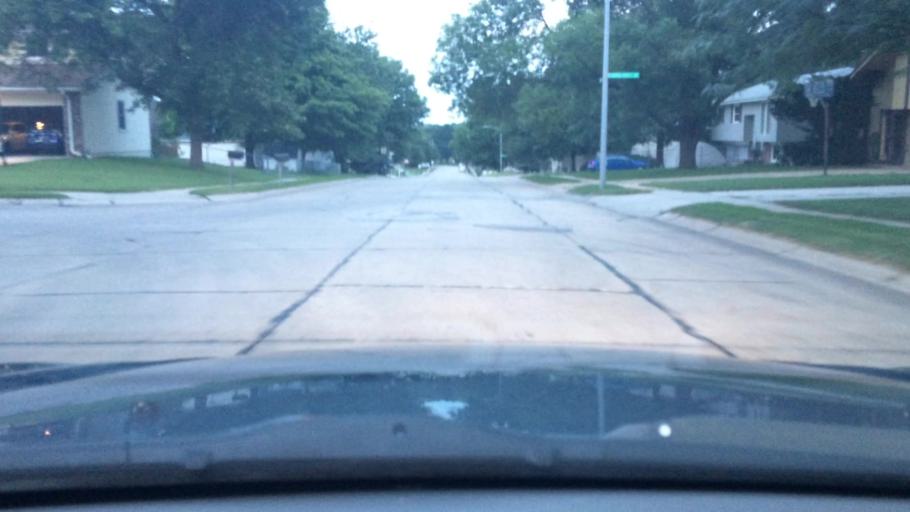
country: US
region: Nebraska
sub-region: Douglas County
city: Ralston
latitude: 41.1839
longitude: -96.0569
